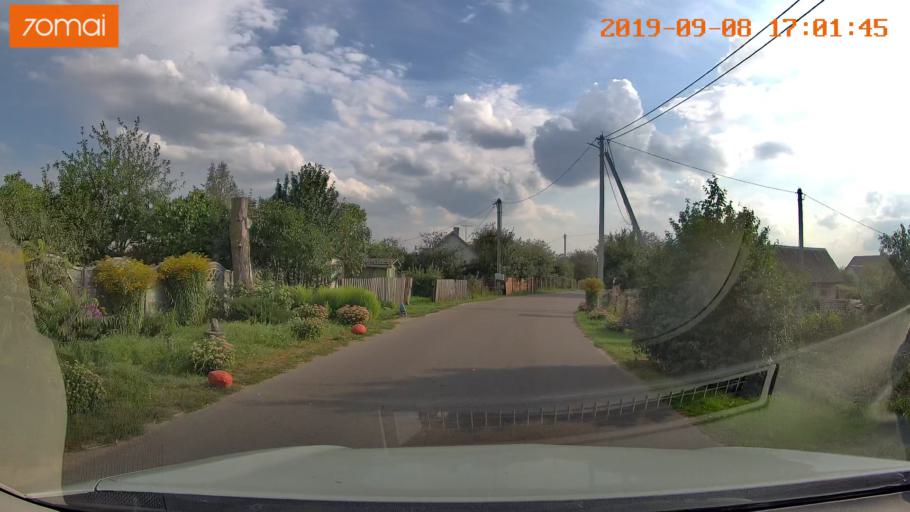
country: BY
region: Grodnenskaya
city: Hrodna
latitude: 53.7080
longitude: 23.9367
